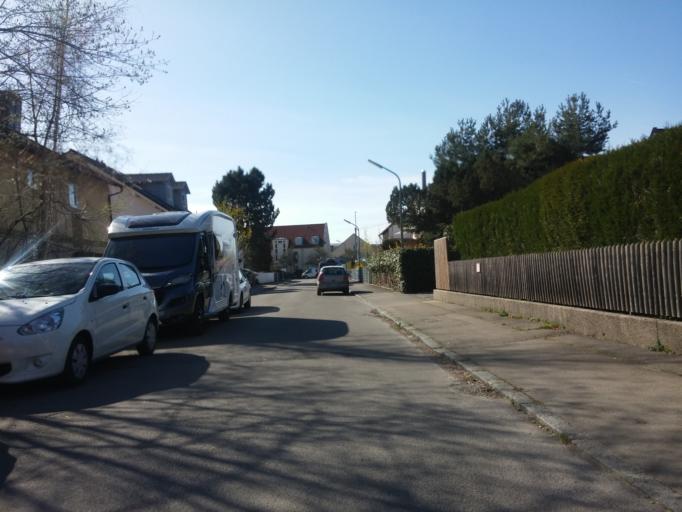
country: DE
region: Bavaria
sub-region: Upper Bavaria
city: Neubiberg
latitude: 48.0814
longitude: 11.6674
